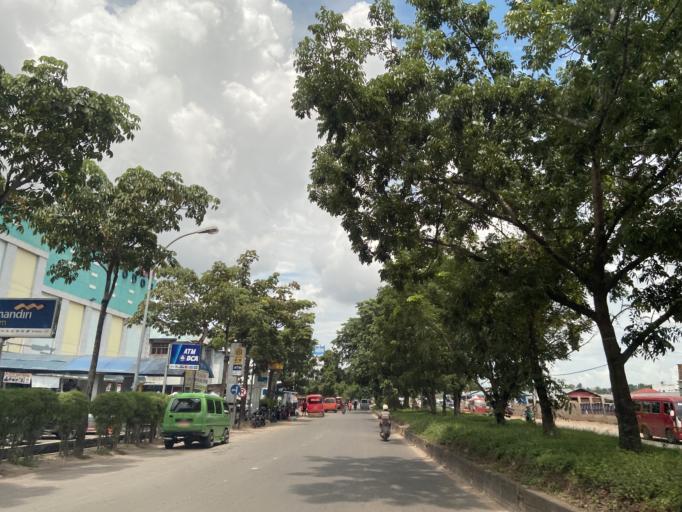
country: SG
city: Singapore
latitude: 1.1473
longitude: 104.0034
